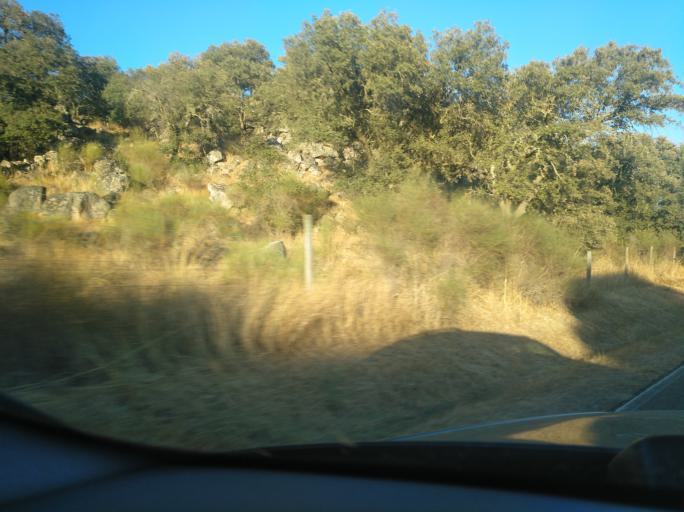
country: PT
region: Portalegre
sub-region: Arronches
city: Arronches
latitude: 39.0704
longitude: -7.2484
